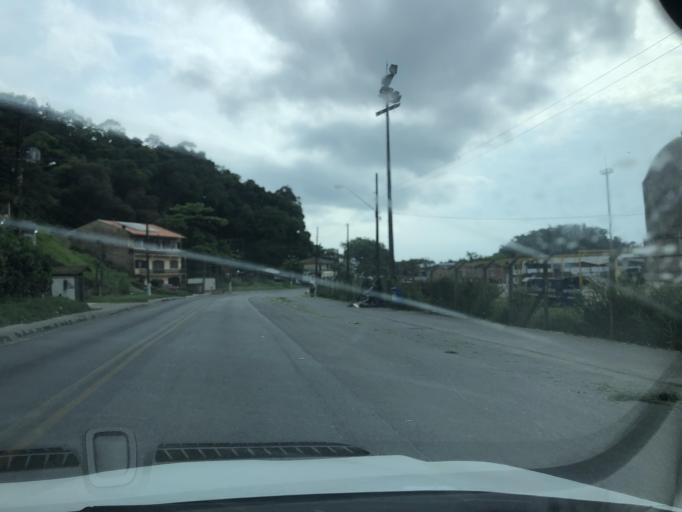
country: BR
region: Santa Catarina
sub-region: Sao Francisco Do Sul
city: Sao Francisco do Sul
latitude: -26.2404
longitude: -48.6326
